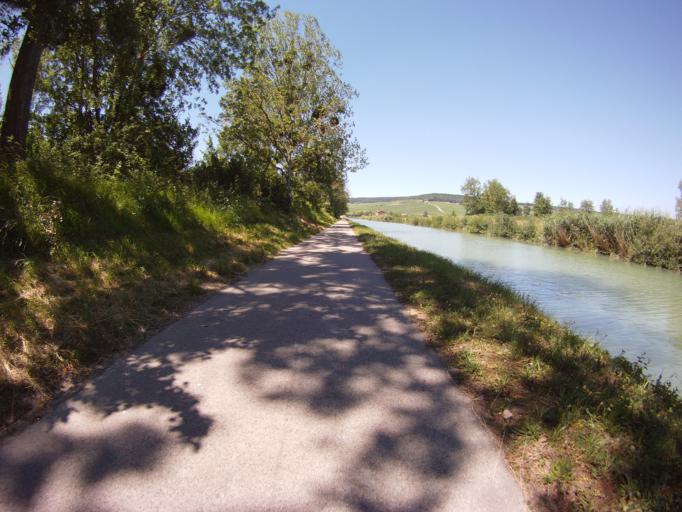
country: FR
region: Champagne-Ardenne
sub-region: Departement de la Marne
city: Dizy
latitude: 49.0644
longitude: 3.9539
